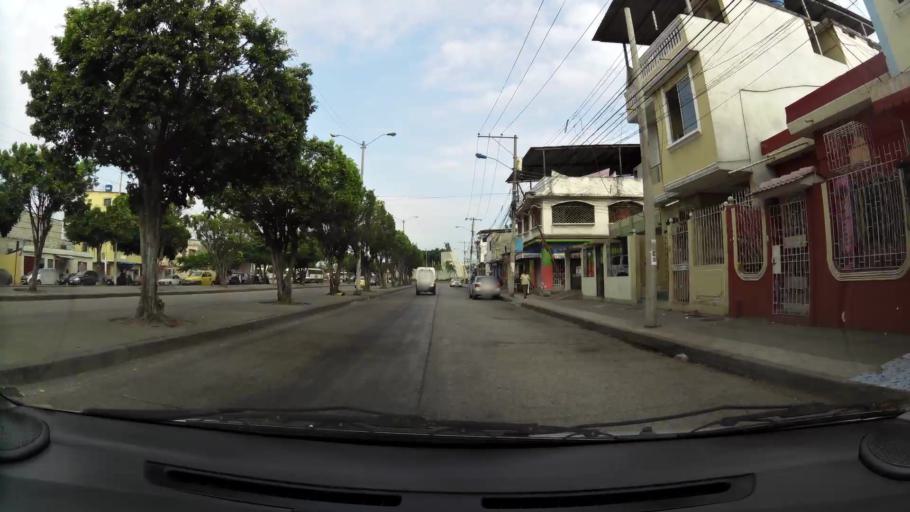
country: EC
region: Guayas
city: Eloy Alfaro
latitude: -2.1311
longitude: -79.8903
